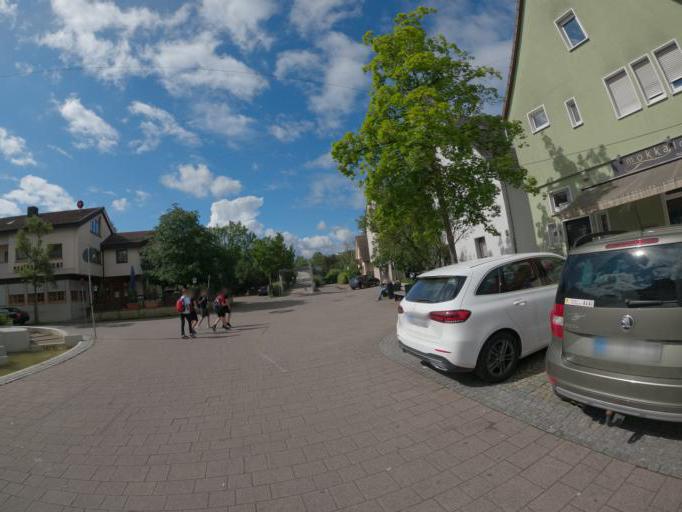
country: DE
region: Baden-Wuerttemberg
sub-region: Regierungsbezirk Stuttgart
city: Ebersbach an der Fils
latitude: 48.7136
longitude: 9.5248
